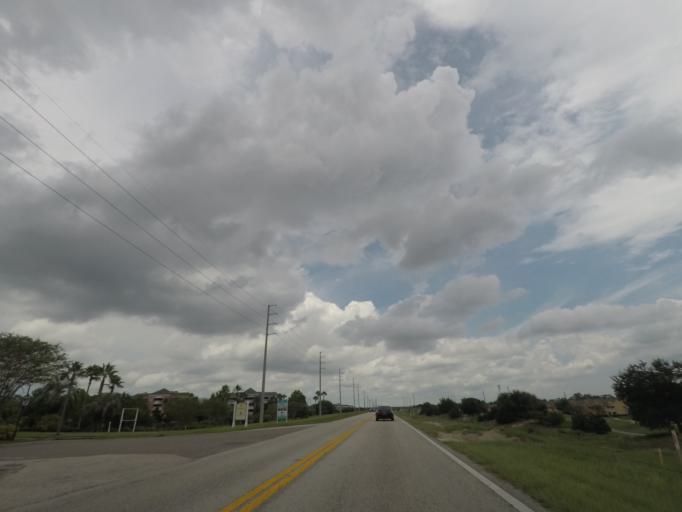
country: US
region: Florida
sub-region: Polk County
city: Loughman
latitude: 28.2754
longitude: -81.5906
